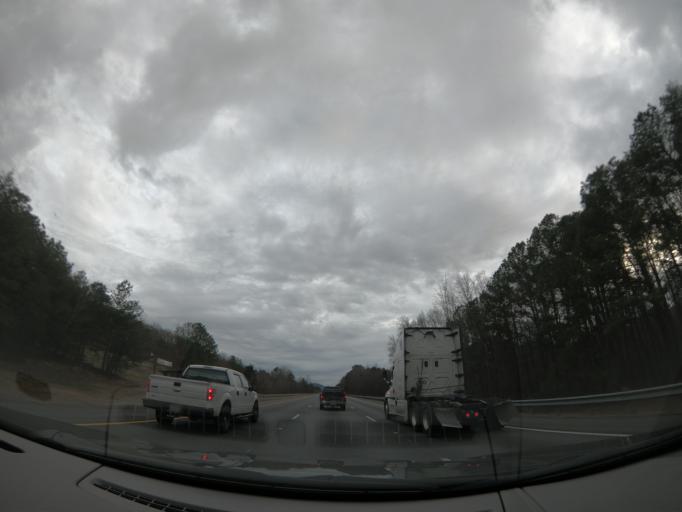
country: US
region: Georgia
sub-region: Whitfield County
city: Varnell
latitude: 34.8459
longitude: -85.0182
